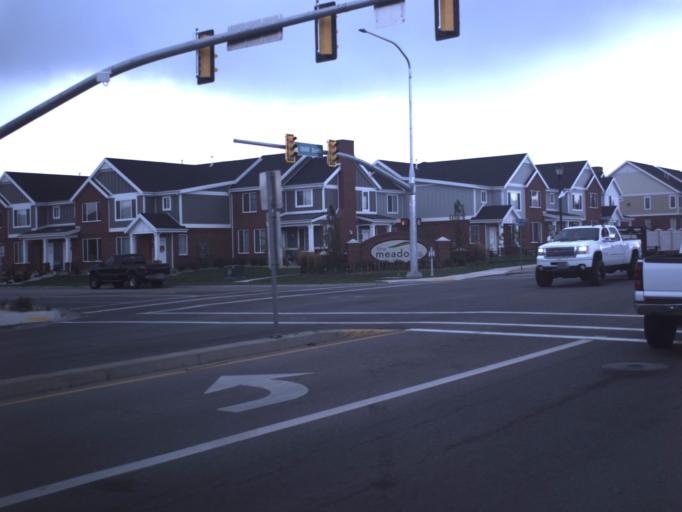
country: US
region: Utah
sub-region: Salt Lake County
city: Riverton
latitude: 40.5224
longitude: -111.9456
